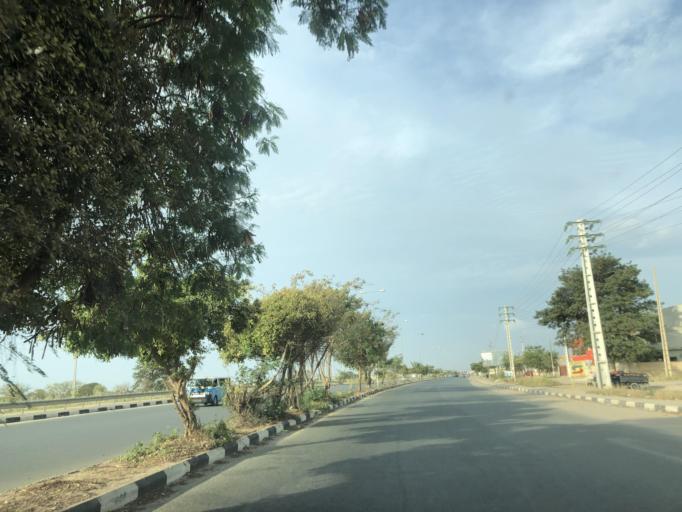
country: AO
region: Luanda
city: Luanda
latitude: -8.9383
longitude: 13.2960
